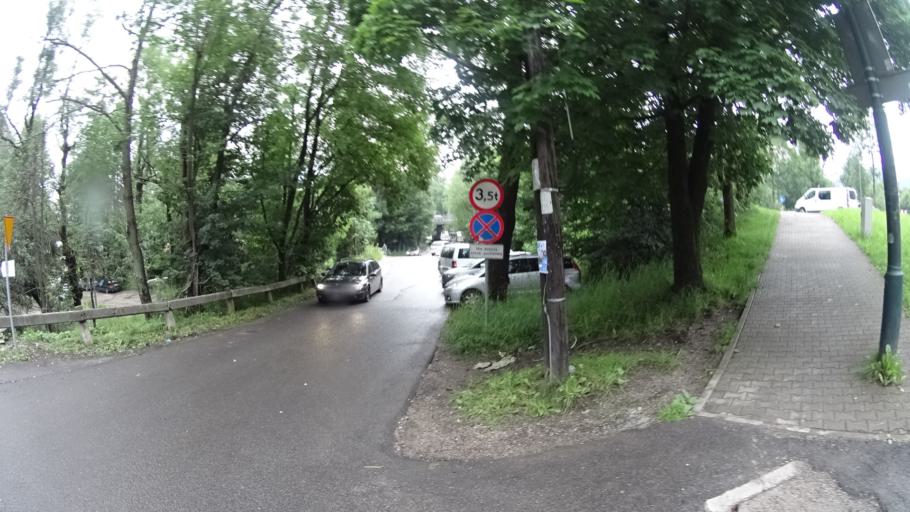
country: PL
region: Lesser Poland Voivodeship
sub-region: Powiat tatrzanski
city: Zakopane
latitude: 49.2963
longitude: 19.9439
